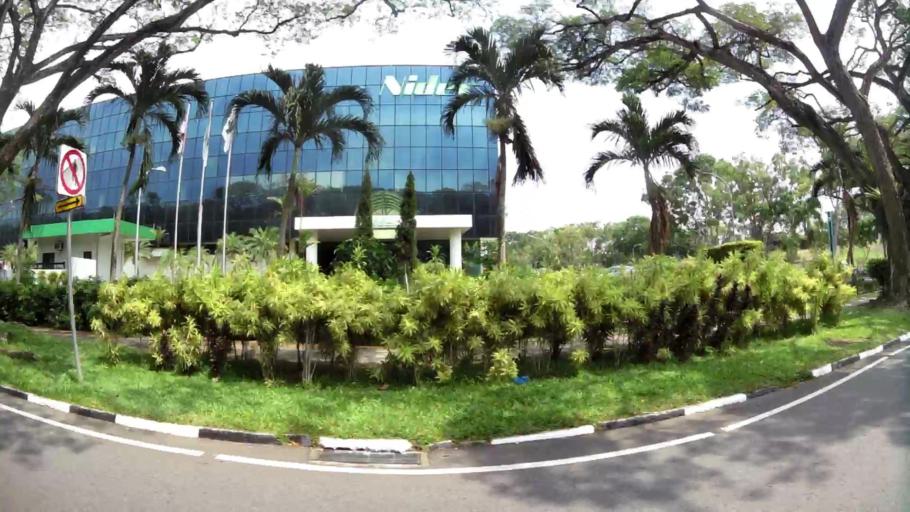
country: MY
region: Johor
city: Kampung Pasir Gudang Baru
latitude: 1.3745
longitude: 103.9746
